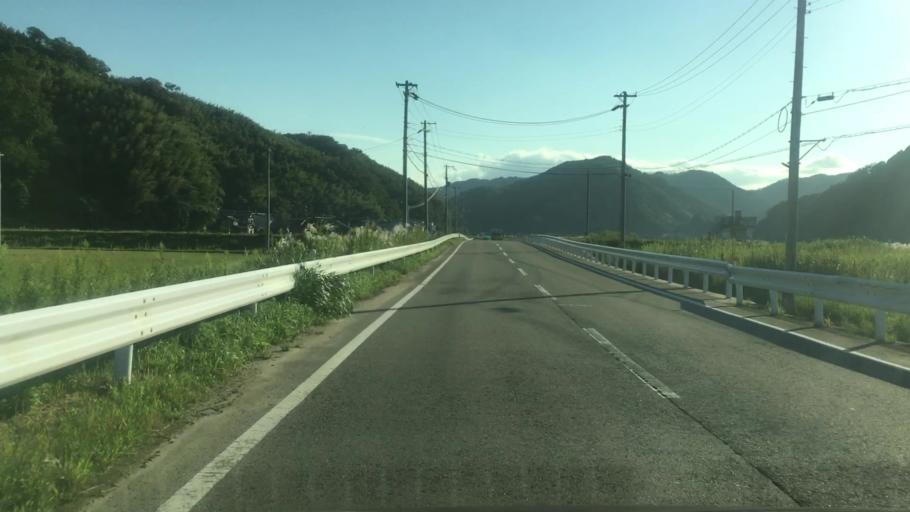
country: JP
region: Hyogo
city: Toyooka
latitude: 35.6160
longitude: 134.8132
